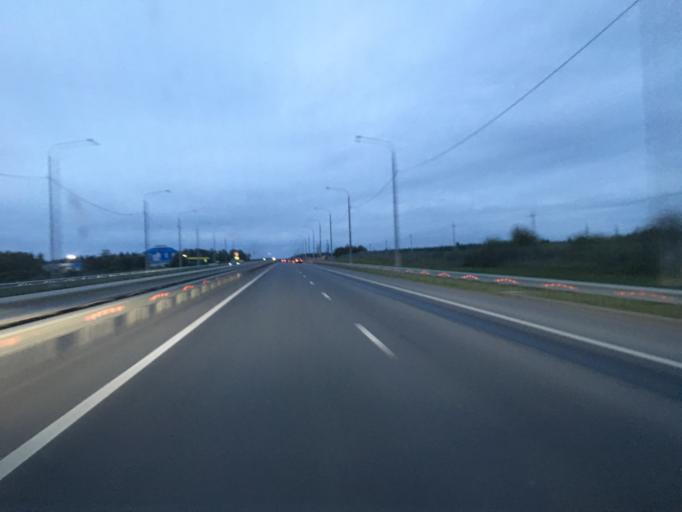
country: RU
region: Kaluga
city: Maloyaroslavets
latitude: 54.9523
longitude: 36.4492
